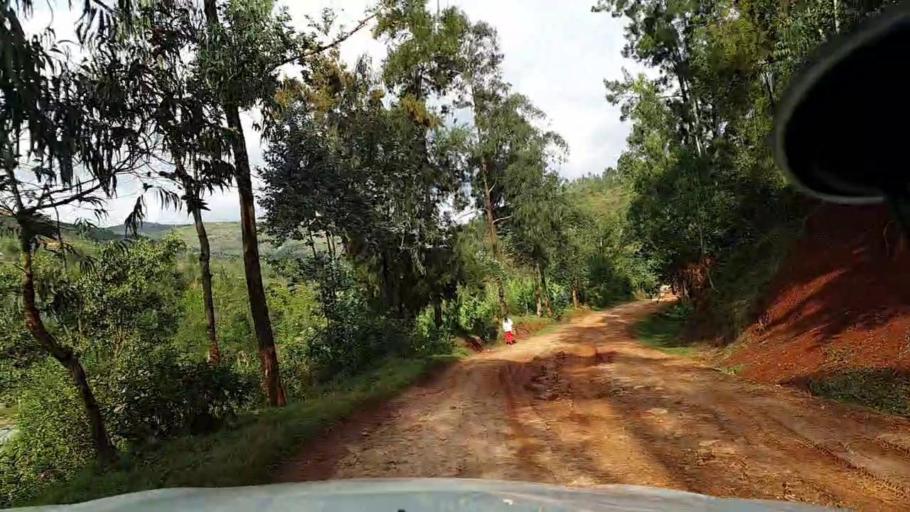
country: RW
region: Southern Province
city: Gitarama
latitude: -2.1638
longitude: 29.5565
